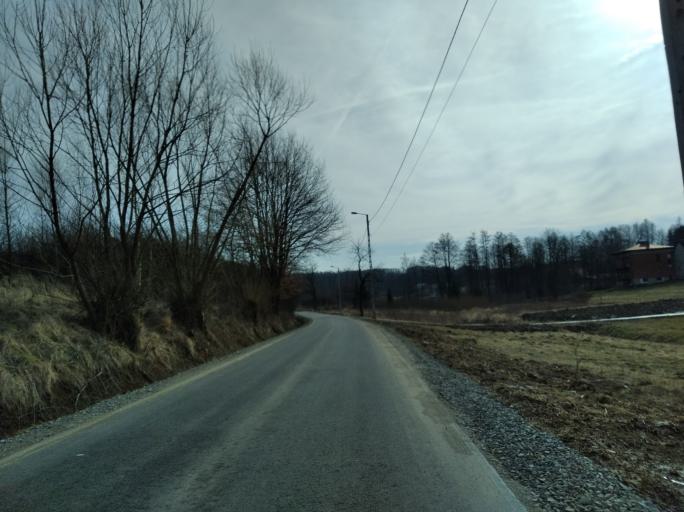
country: PL
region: Subcarpathian Voivodeship
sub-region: Powiat brzozowski
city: Jasienica Rosielna
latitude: 49.7614
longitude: 21.9463
